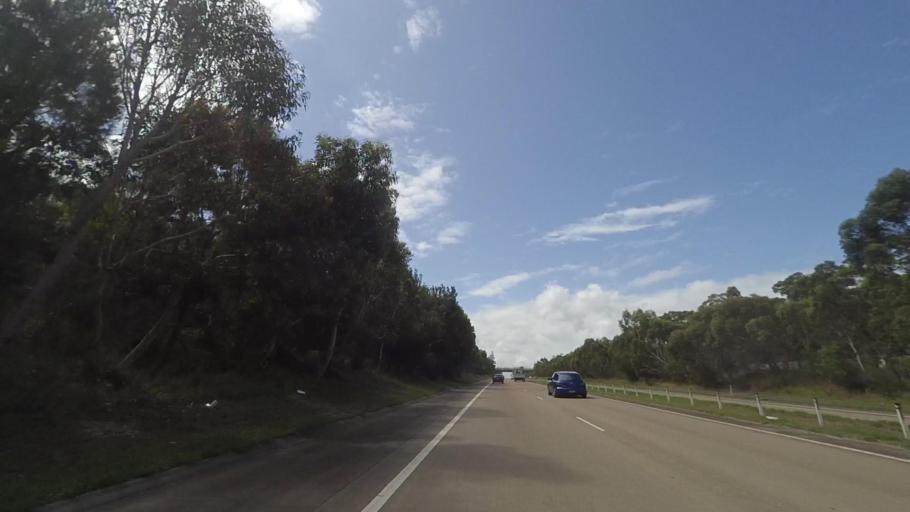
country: AU
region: New South Wales
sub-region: Lake Macquarie Shire
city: Gateshead
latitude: -32.9782
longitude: 151.6792
